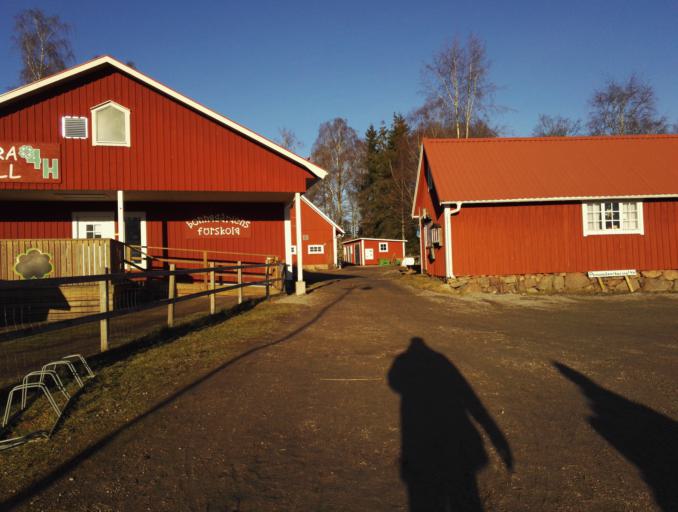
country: SE
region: Kronoberg
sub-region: Vaxjo Kommun
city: Vaexjoe
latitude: 56.9176
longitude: 14.7955
